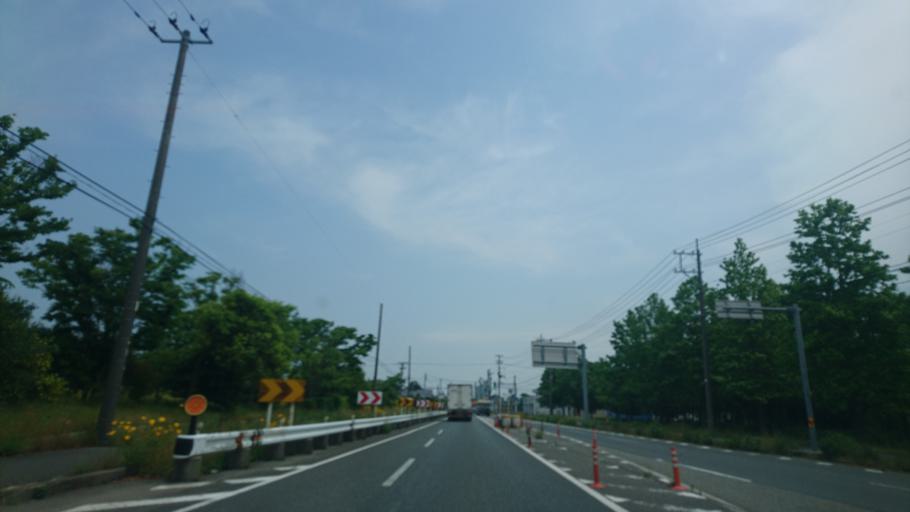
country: JP
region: Niigata
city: Shibata
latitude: 37.9980
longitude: 139.2555
